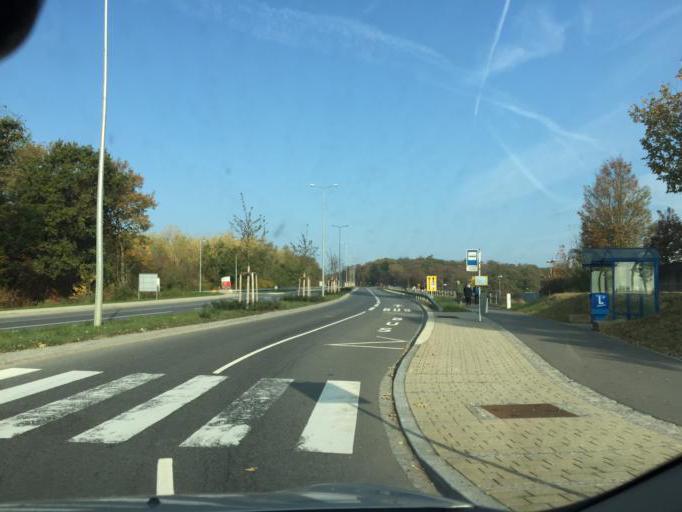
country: LU
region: Luxembourg
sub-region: Canton de Luxembourg
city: Sandweiler
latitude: 49.5966
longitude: 6.2138
